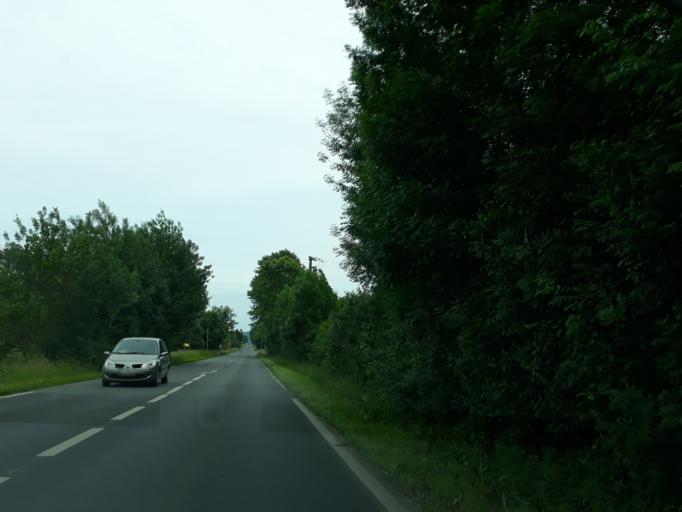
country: FR
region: Limousin
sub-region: Departement de la Correze
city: Cublac
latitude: 45.1274
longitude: 1.3471
